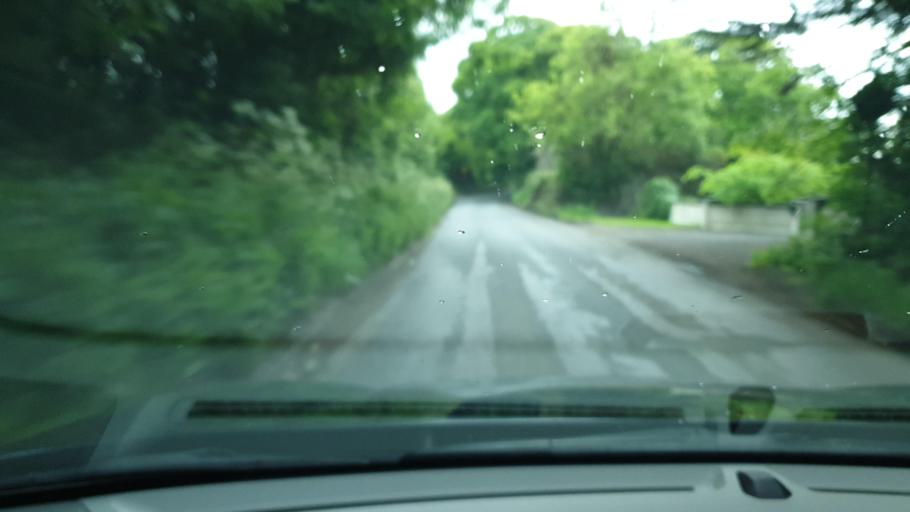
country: IE
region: Leinster
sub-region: An Mhi
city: Ashbourne
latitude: 53.5472
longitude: -6.4085
